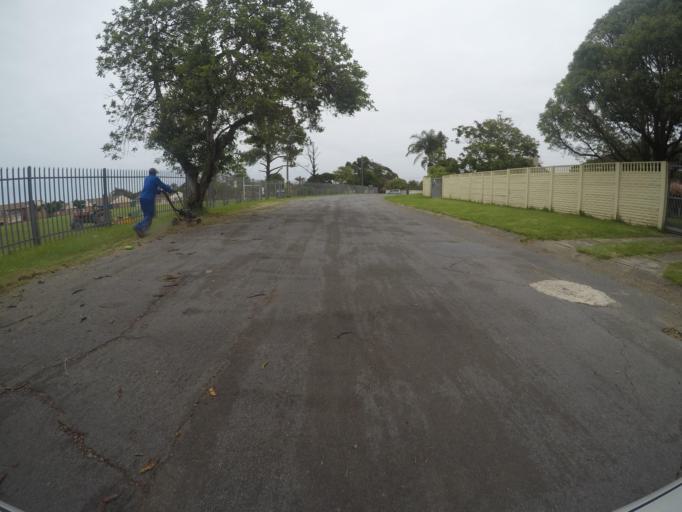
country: ZA
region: Eastern Cape
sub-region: Buffalo City Metropolitan Municipality
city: East London
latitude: -32.9692
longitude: 27.9360
